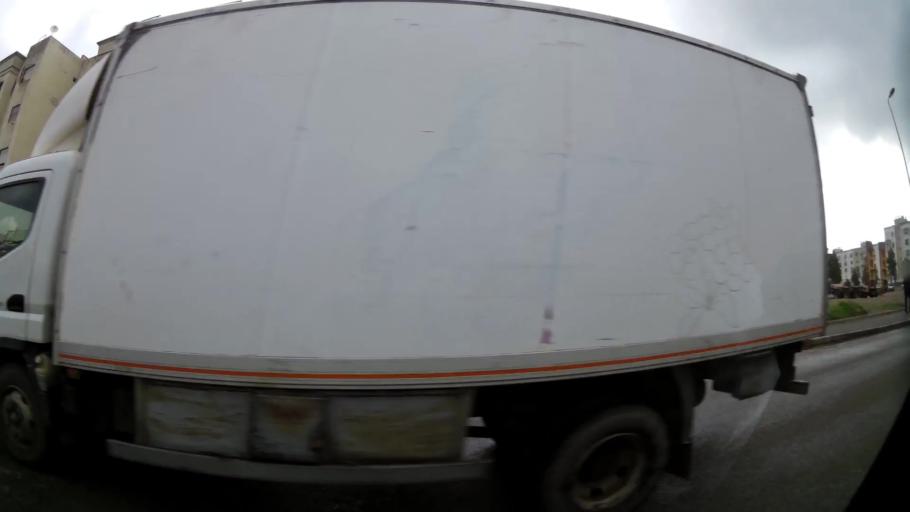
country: MA
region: Grand Casablanca
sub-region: Mediouna
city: Tit Mellil
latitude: 33.5883
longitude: -7.5243
